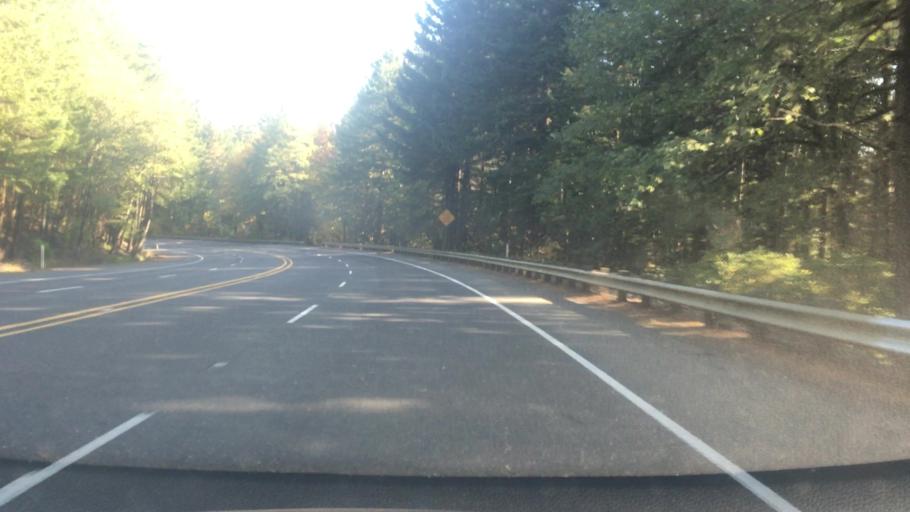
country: US
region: Oregon
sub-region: Polk County
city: Grand Ronde
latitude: 45.0577
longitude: -123.6817
